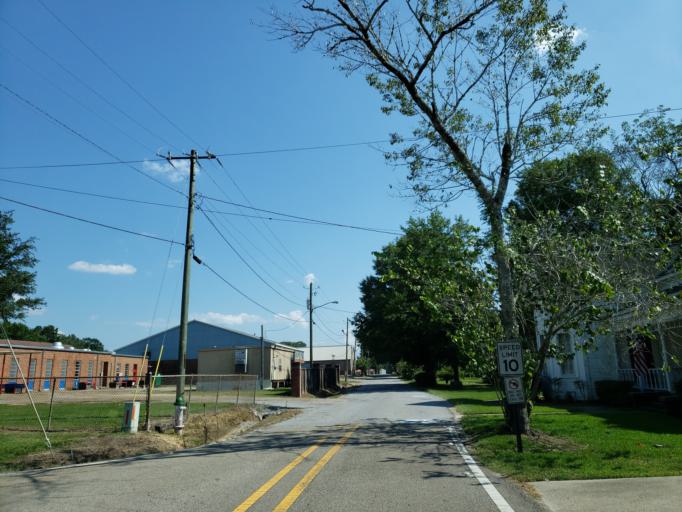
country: US
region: Mississippi
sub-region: Covington County
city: Collins
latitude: 31.5618
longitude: -89.5005
